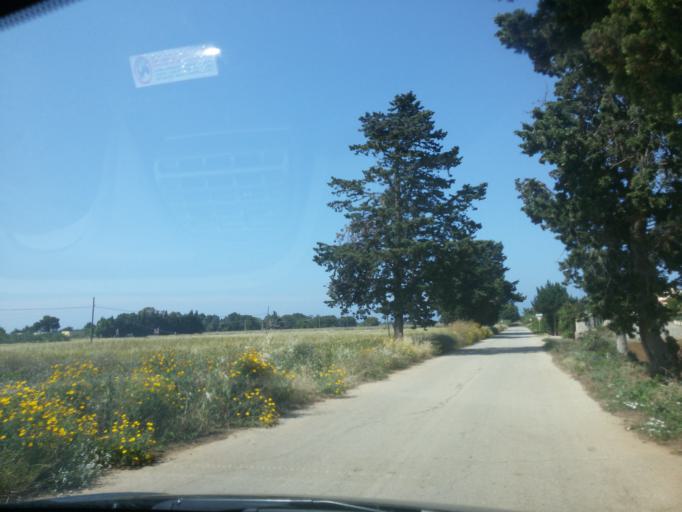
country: IT
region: Apulia
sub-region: Provincia di Brindisi
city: Brindisi
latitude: 40.6666
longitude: 17.8618
